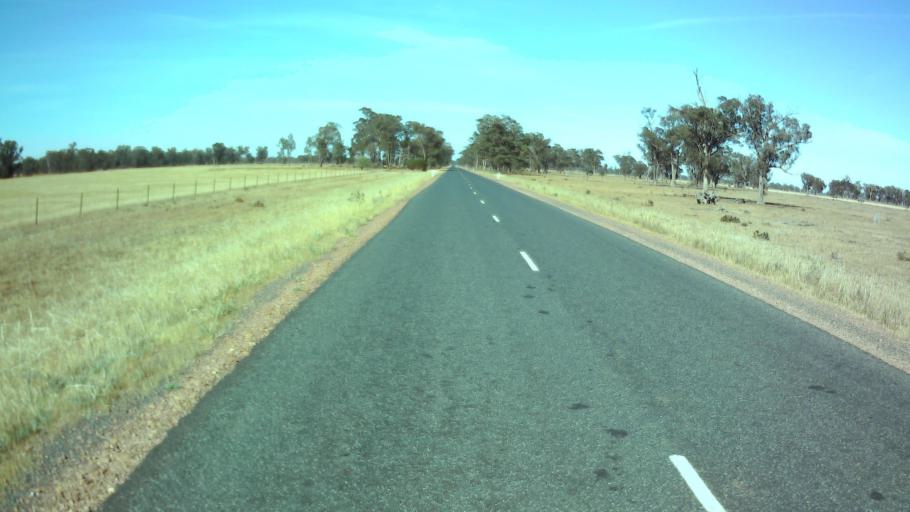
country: AU
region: New South Wales
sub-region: Weddin
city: Grenfell
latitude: -34.1001
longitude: 147.8778
